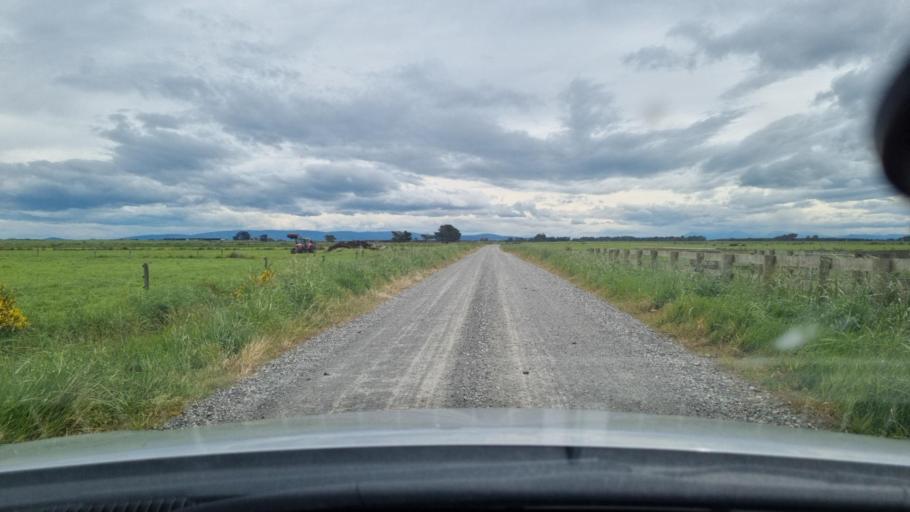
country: NZ
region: Southland
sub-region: Invercargill City
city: Invercargill
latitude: -46.4025
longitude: 168.2866
